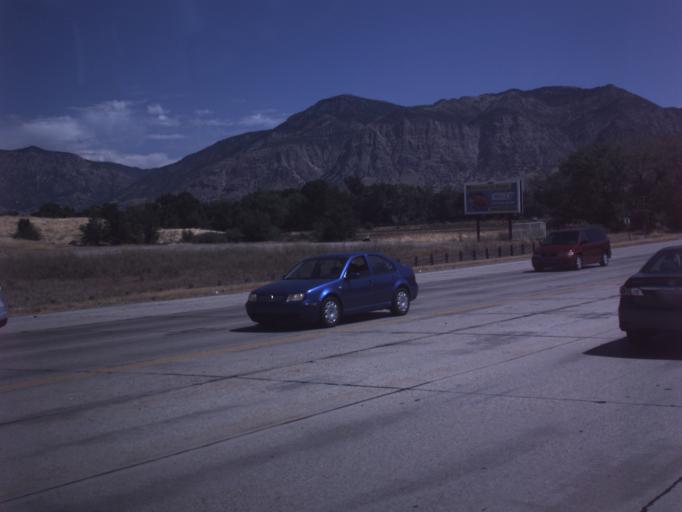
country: US
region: Utah
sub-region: Weber County
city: Ogden
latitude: 41.2298
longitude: -111.9970
